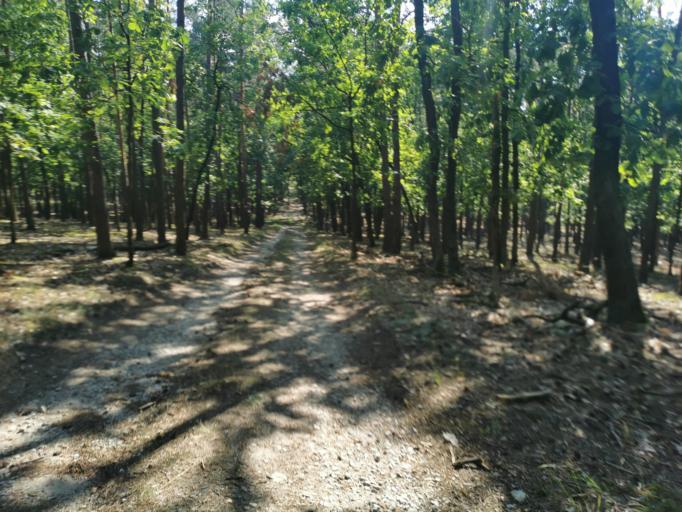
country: SK
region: Trnavsky
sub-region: Okres Senica
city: Senica
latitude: 48.6246
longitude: 17.2812
